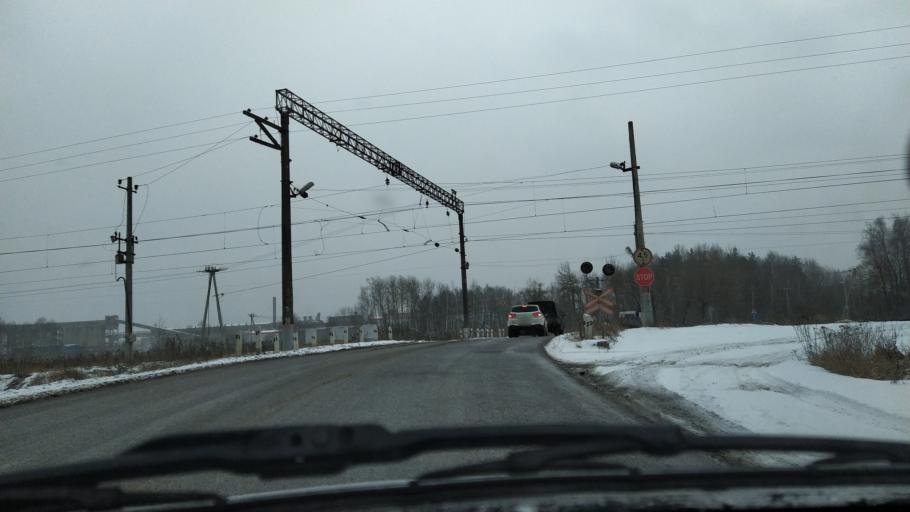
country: RU
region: Moskovskaya
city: Lopatinskiy
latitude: 55.3569
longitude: 38.7373
